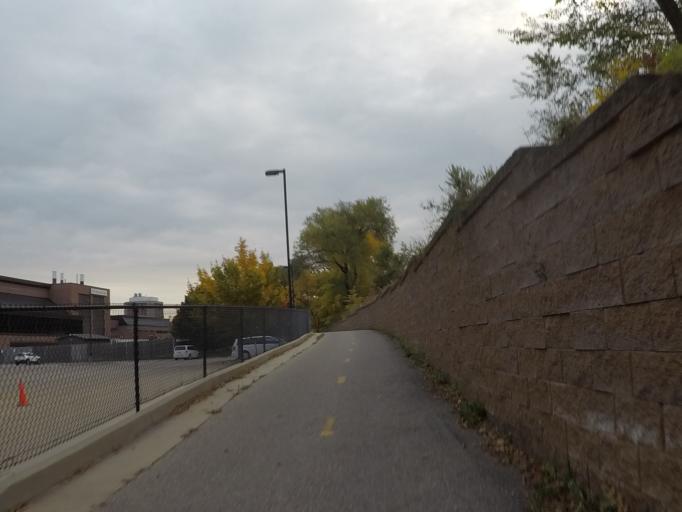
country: US
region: Wisconsin
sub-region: Dane County
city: Madison
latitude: 43.0741
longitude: -89.4214
